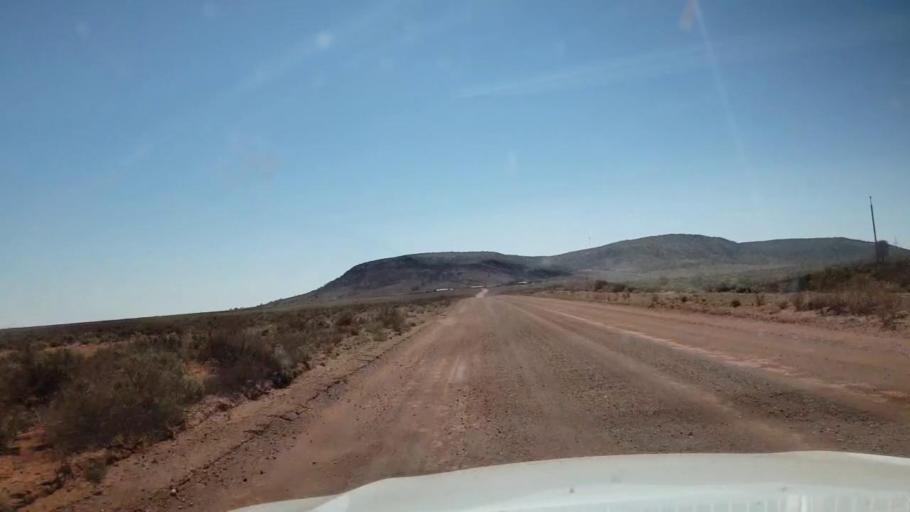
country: AU
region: South Australia
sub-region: Whyalla
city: Whyalla
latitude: -32.6981
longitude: 137.1328
